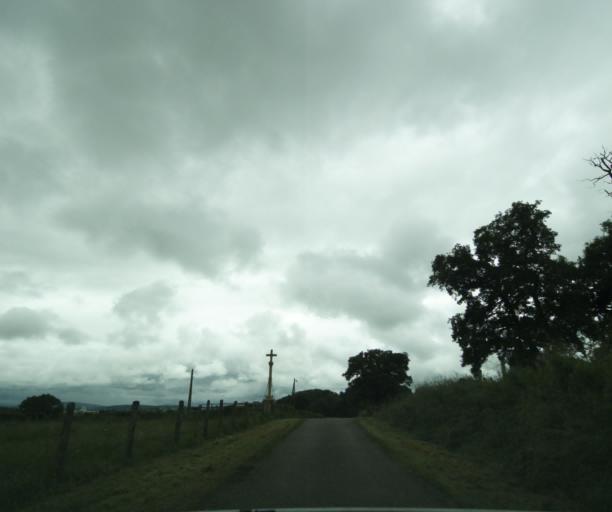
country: FR
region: Bourgogne
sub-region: Departement de Saone-et-Loire
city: Charolles
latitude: 46.4617
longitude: 4.2908
